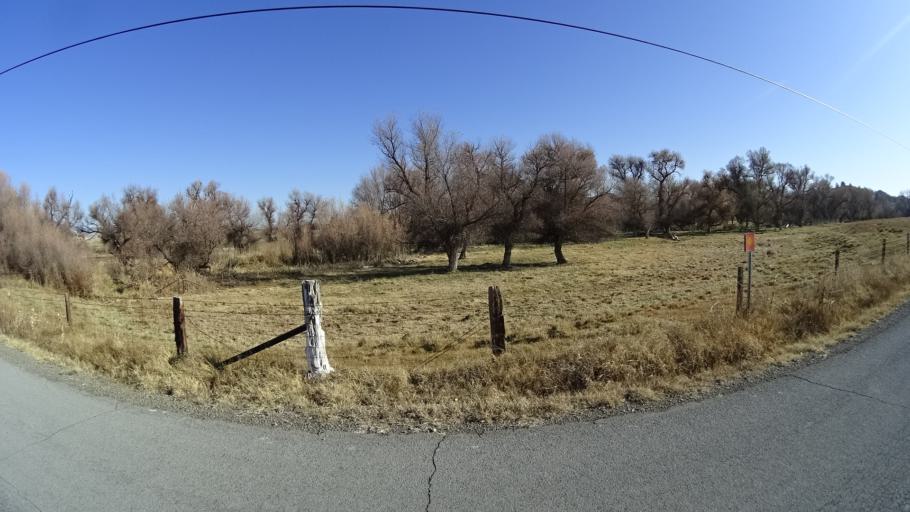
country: US
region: California
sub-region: Siskiyou County
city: Montague
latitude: 41.7042
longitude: -122.5373
